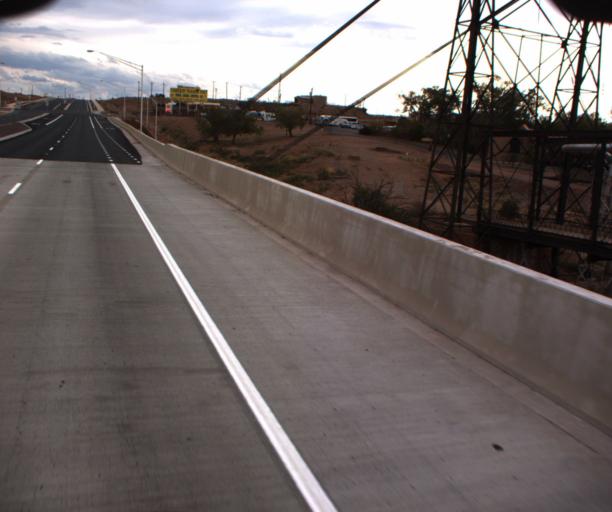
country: US
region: Arizona
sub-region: Coconino County
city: Tuba City
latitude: 35.8765
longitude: -111.4117
